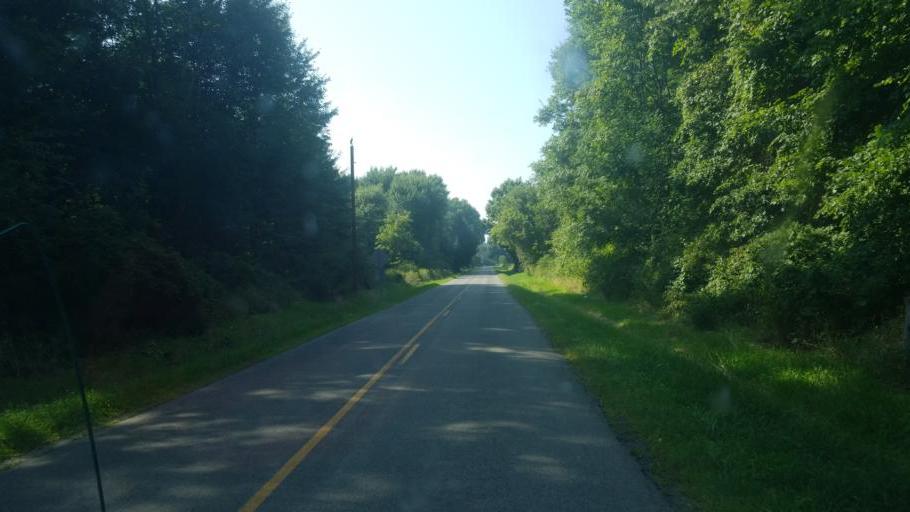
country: US
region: Ohio
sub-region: Medina County
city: Lodi
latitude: 41.0143
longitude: -82.0357
